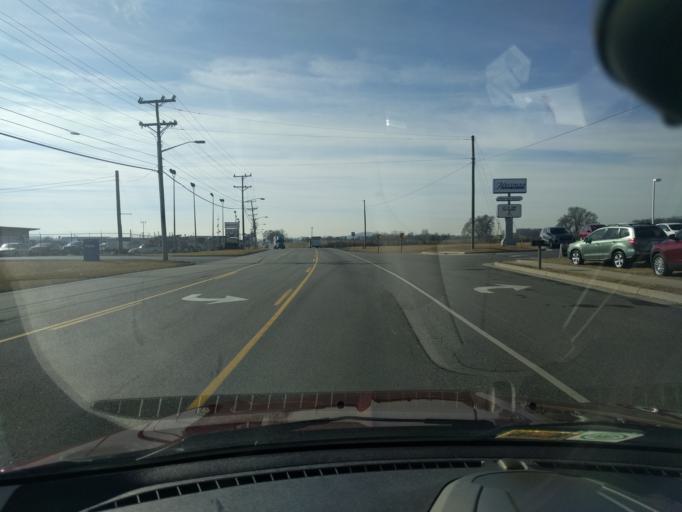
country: US
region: Virginia
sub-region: Rockingham County
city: Dayton
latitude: 38.4030
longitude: -78.9109
